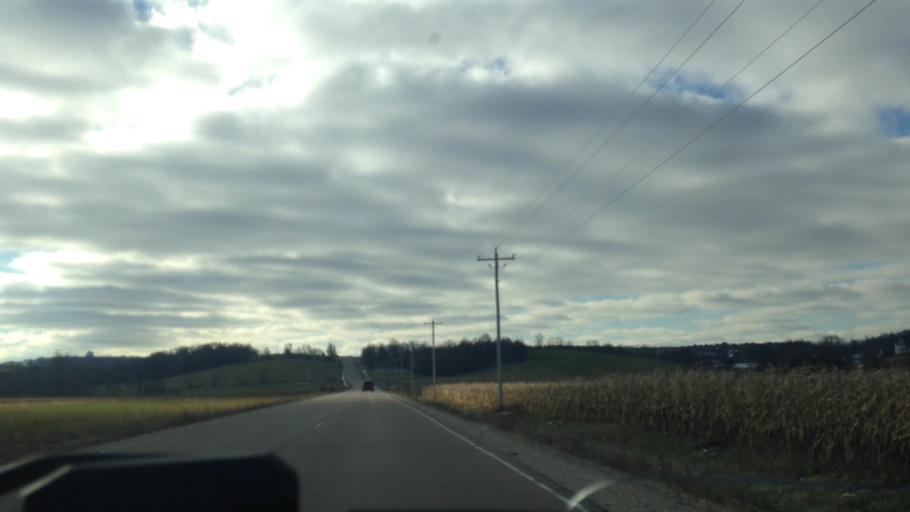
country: US
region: Wisconsin
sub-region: Dodge County
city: Mayville
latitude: 43.4678
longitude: -88.5001
